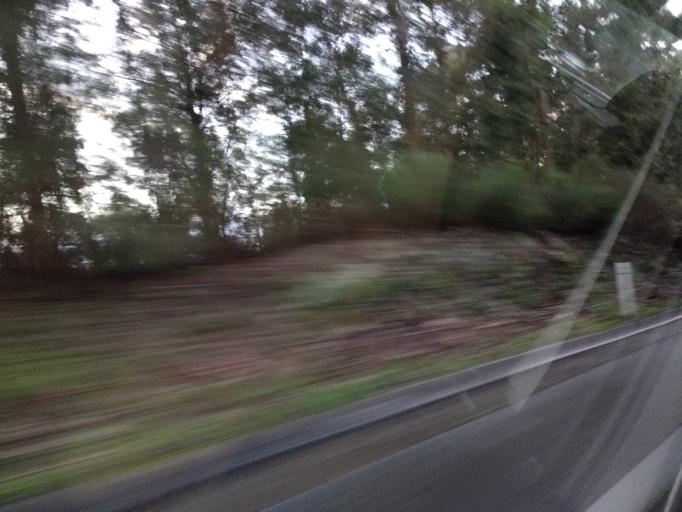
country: PT
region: Braga
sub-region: Braga
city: Oliveira
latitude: 41.4668
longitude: -8.4704
